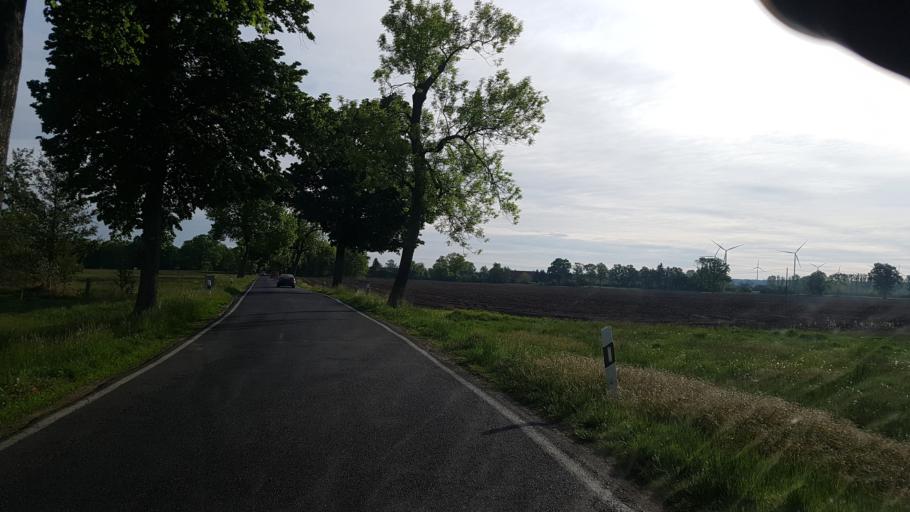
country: DE
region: Brandenburg
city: Dahme
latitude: 51.8811
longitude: 13.4523
